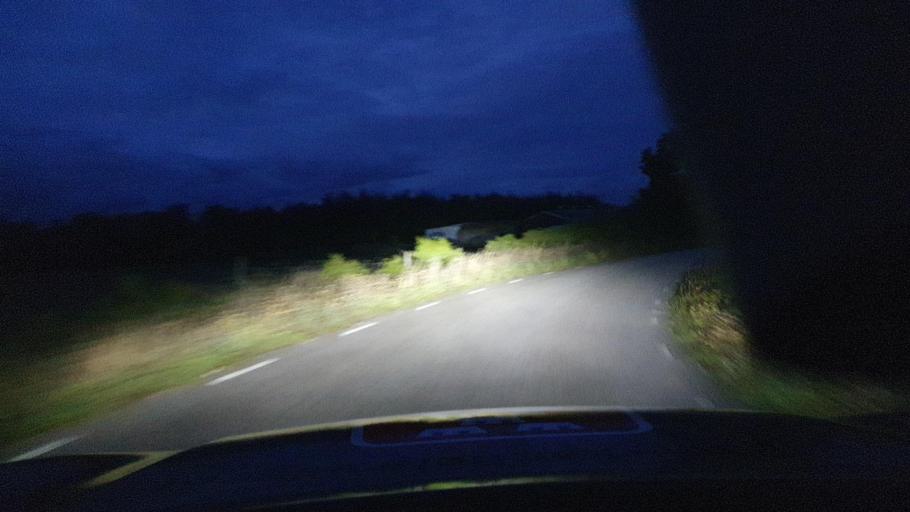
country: SE
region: Gotland
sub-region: Gotland
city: Slite
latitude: 57.8353
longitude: 18.6715
